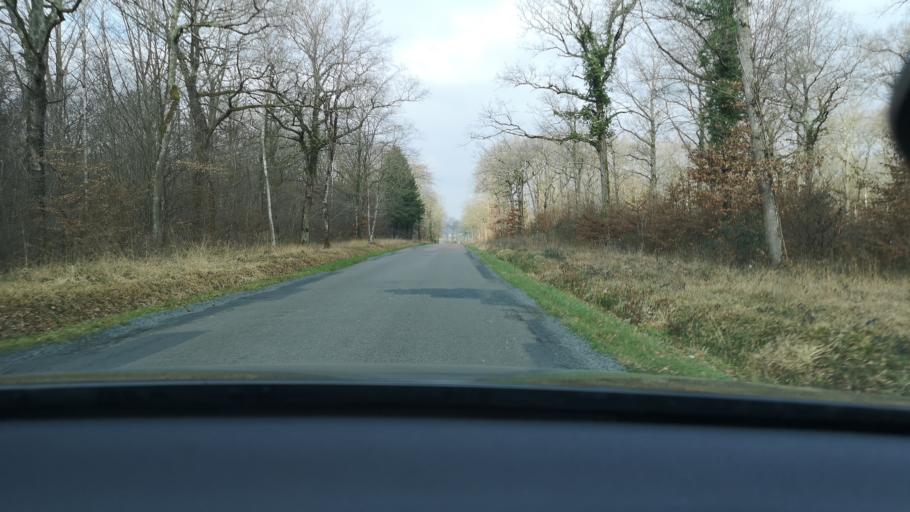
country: FR
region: Bourgogne
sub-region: Departement de Saone-et-Loire
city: Dracy-le-Fort
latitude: 46.7689
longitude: 4.7693
